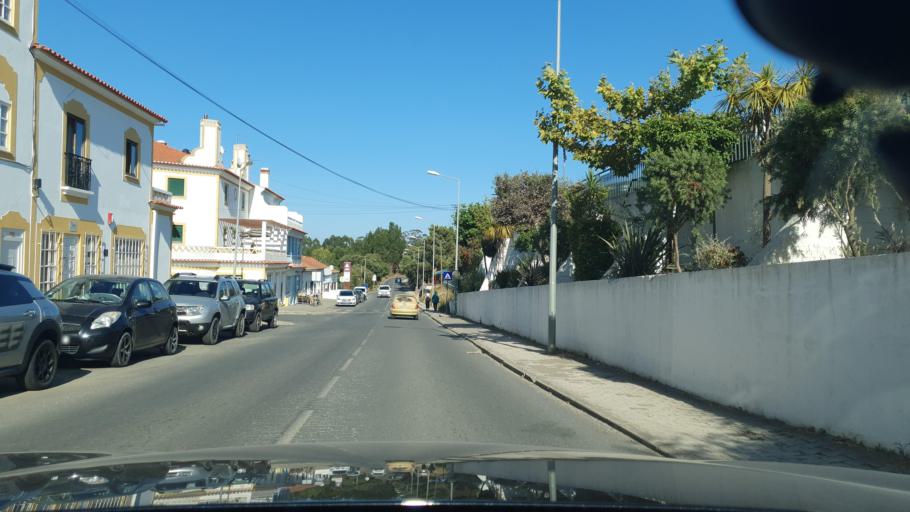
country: PT
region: Beja
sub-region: Odemira
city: Sao Teotonio
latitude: 37.5100
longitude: -8.7149
